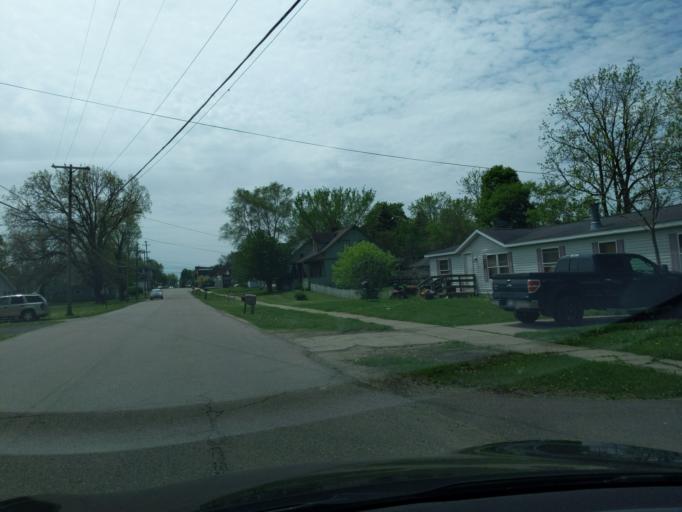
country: US
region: Michigan
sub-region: Ingham County
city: Stockbridge
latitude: 42.4539
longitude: -84.1802
